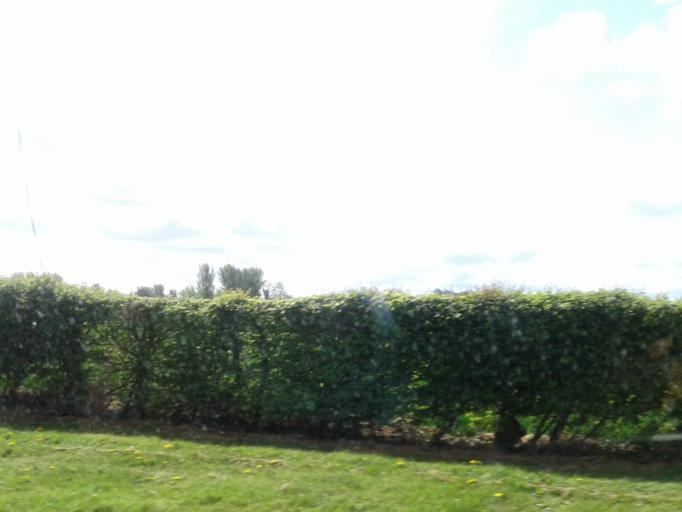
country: IE
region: Leinster
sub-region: Fingal County
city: Swords
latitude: 53.4738
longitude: -6.2596
